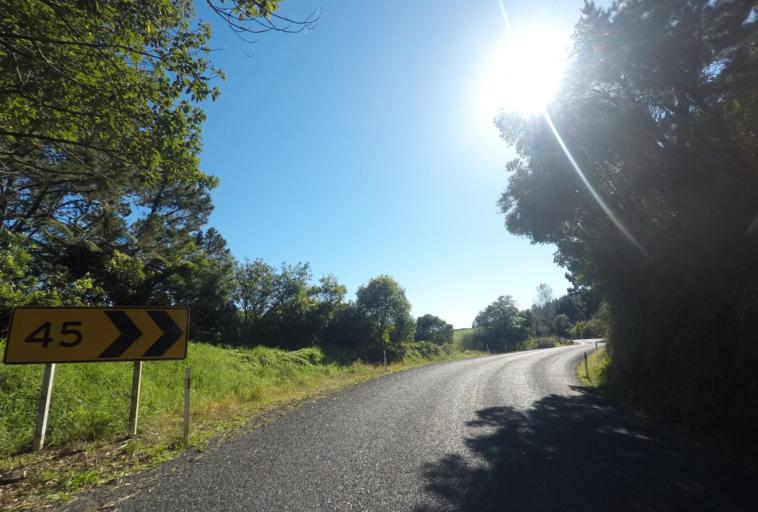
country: NZ
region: Bay of Plenty
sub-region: Western Bay of Plenty District
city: Waihi Beach
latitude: -37.3920
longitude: 175.9044
